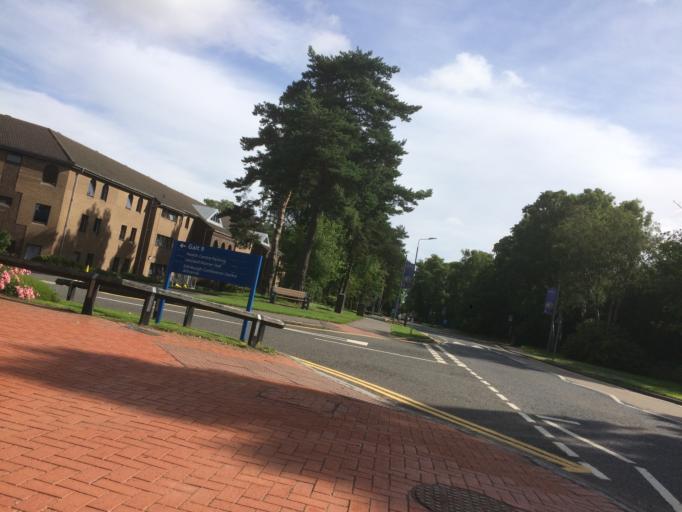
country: GB
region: Scotland
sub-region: Edinburgh
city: Currie
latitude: 55.9098
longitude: -3.3185
